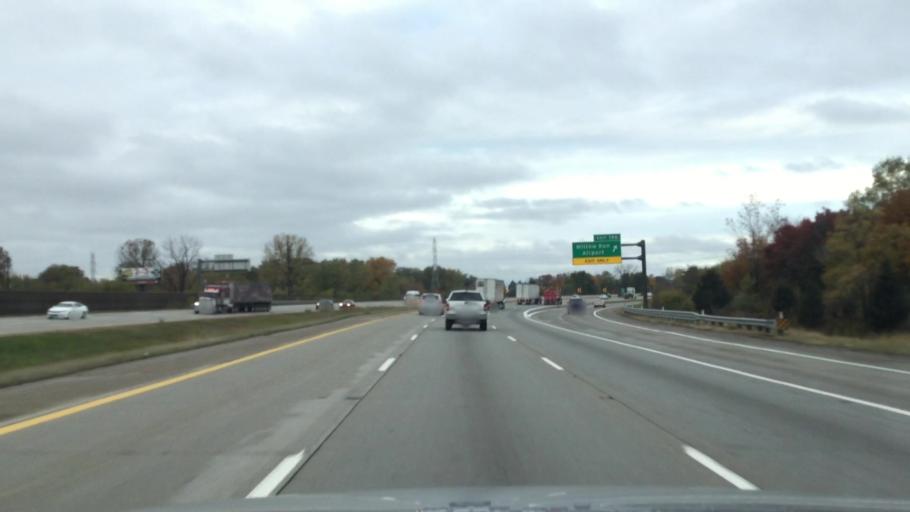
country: US
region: Michigan
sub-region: Washtenaw County
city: Ypsilanti
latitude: 42.2178
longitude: -83.5538
